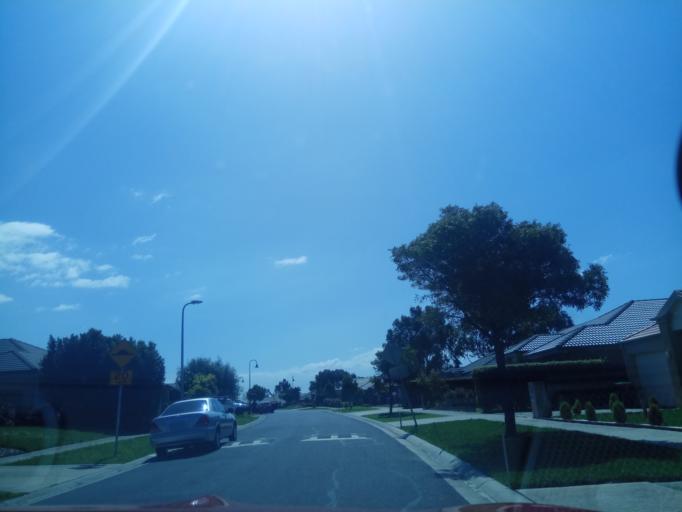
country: AU
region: Victoria
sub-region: Casey
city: Lynbrook
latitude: -38.0633
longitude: 145.2480
